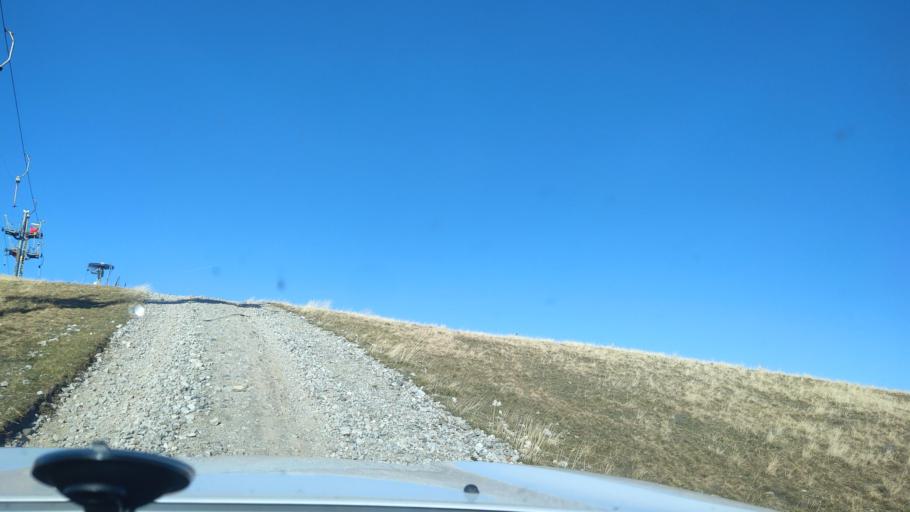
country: FR
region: Rhone-Alpes
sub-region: Departement de la Savoie
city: Saint-Etienne-de-Cuines
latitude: 45.2380
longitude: 6.2362
